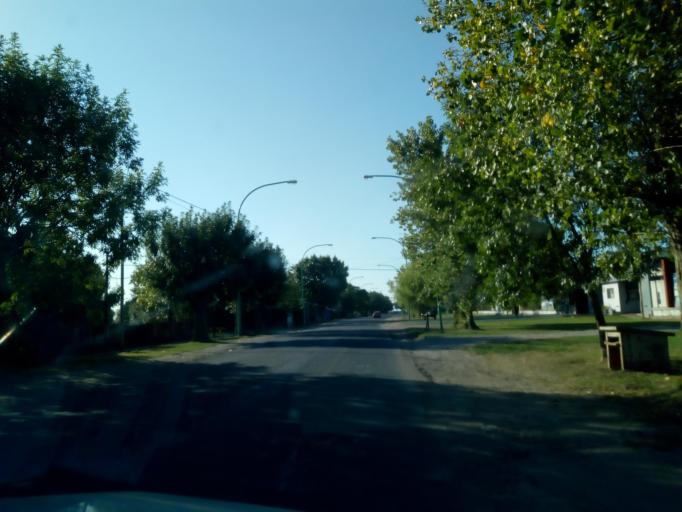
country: AR
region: Buenos Aires
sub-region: Partido de Ensenada
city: Ensenada
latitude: -34.8118
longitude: -57.9805
